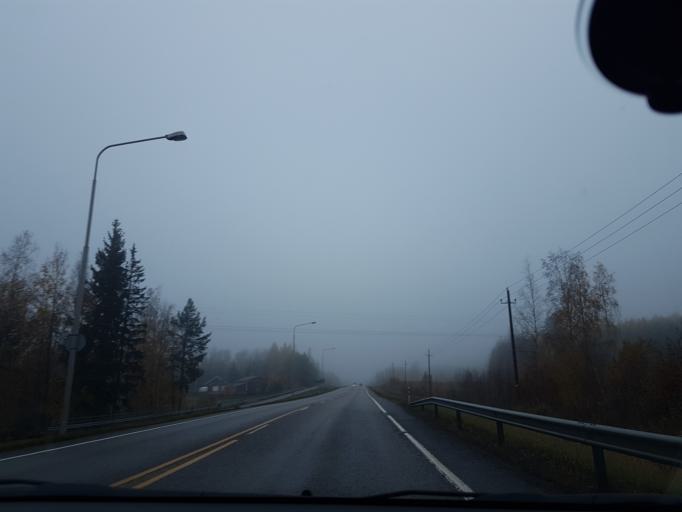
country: FI
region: Uusimaa
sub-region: Helsinki
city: Jaervenpaeae
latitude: 60.4531
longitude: 25.1363
